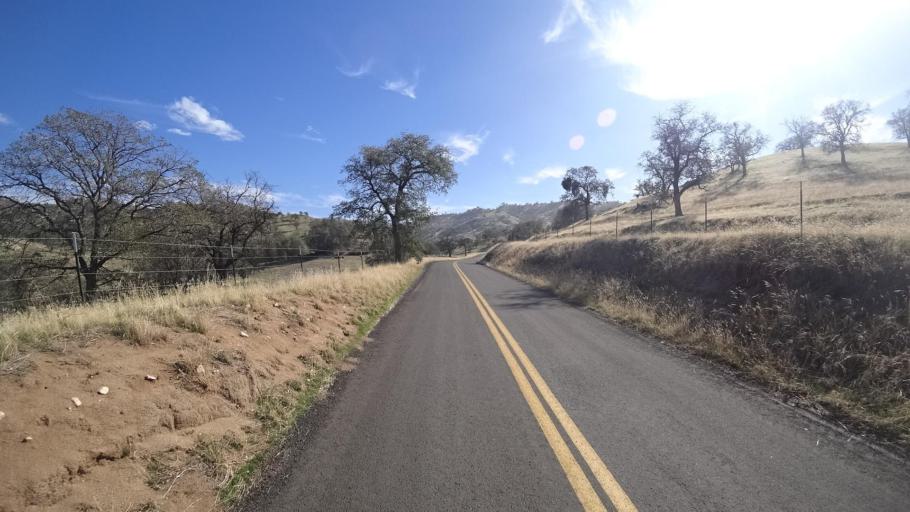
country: US
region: California
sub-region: Kern County
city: Alta Sierra
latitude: 35.6948
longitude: -118.8366
